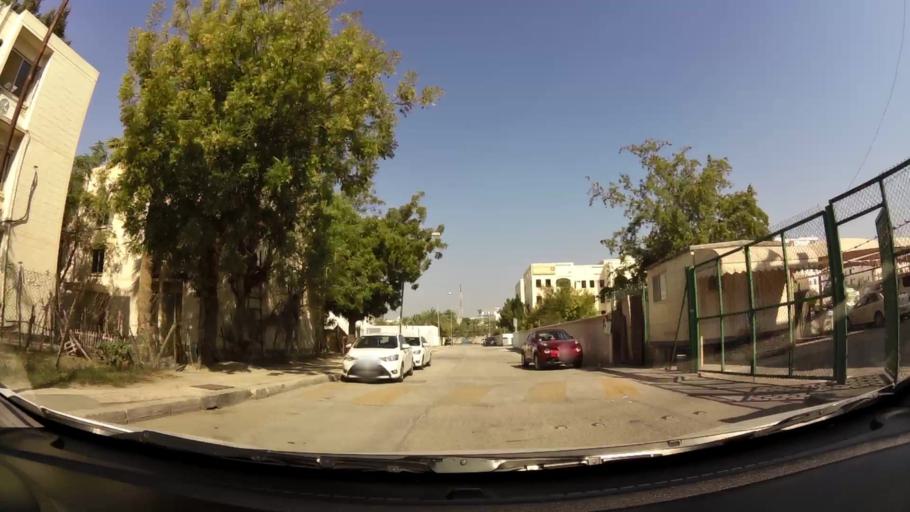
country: BH
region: Manama
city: Manama
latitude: 26.2107
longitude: 50.5907
